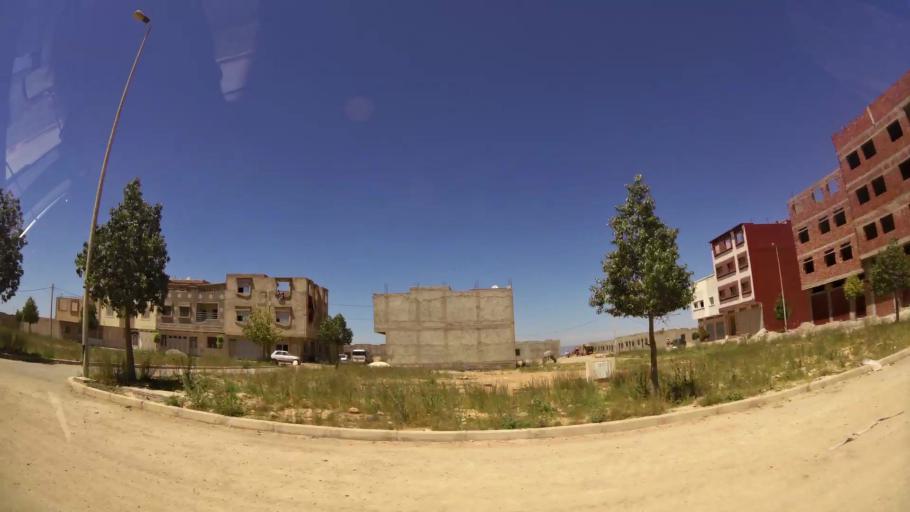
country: MA
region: Oriental
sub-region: Oujda-Angad
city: Oujda
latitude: 34.6814
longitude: -1.8565
